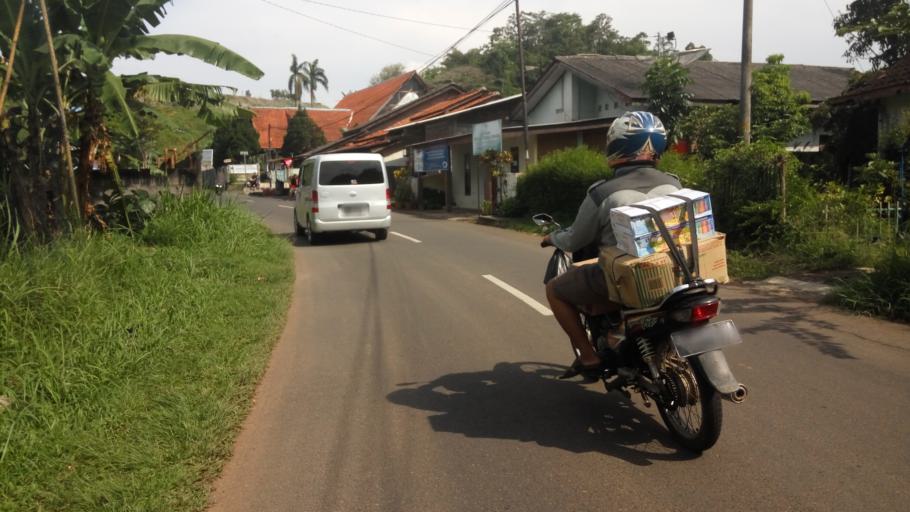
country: ID
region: Central Java
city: Ungaran
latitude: -7.1270
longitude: 110.4211
